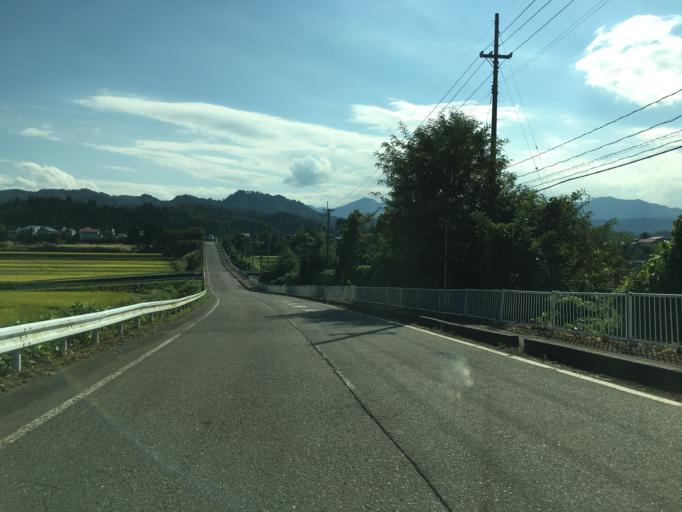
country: JP
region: Fukushima
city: Kitakata
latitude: 37.5857
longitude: 139.6565
